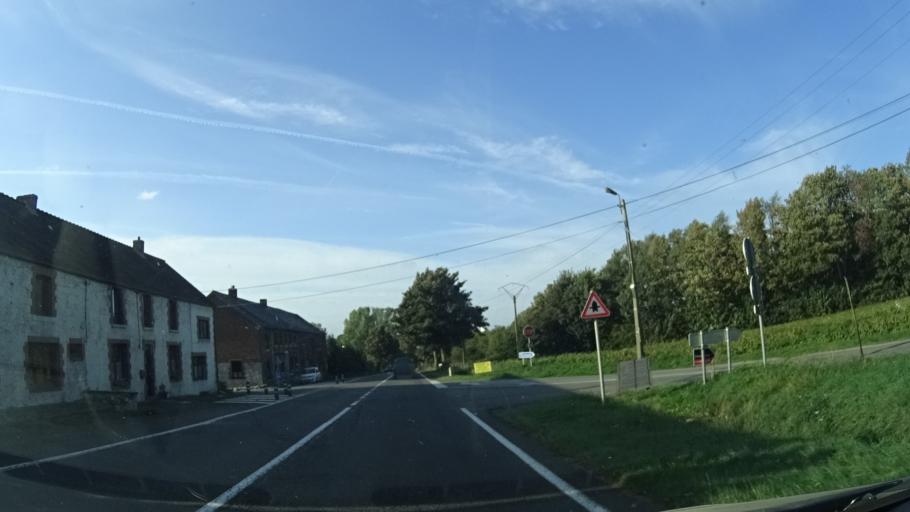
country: BE
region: Wallonia
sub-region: Province du Hainaut
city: Beaumont
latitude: 50.2702
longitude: 4.2139
